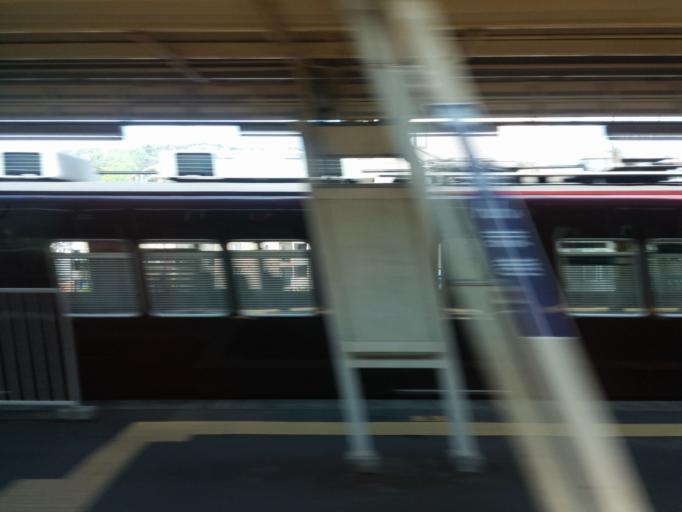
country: JP
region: Kyoto
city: Yawata
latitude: 34.8718
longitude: 135.6614
